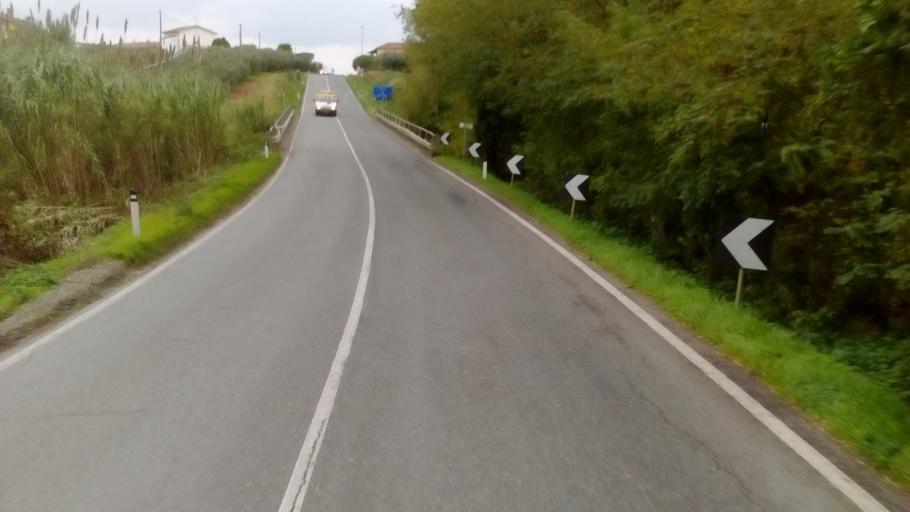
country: IT
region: Abruzzo
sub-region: Provincia di Chieti
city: Vasto
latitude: 42.1651
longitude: 14.6770
